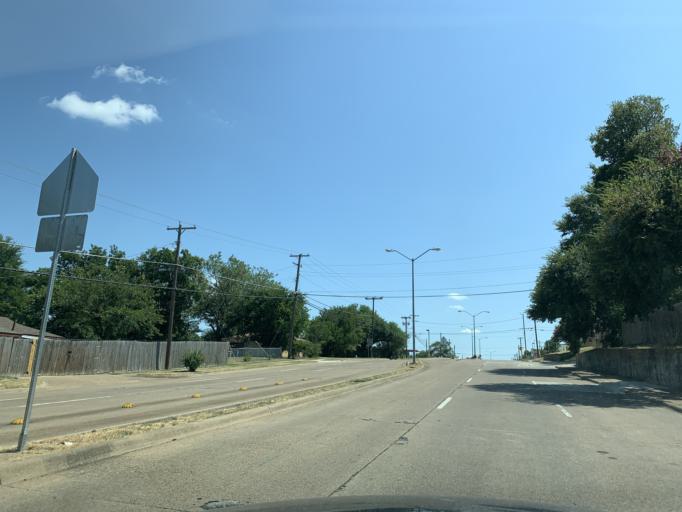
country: US
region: Texas
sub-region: Dallas County
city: Hutchins
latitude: 32.6772
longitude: -96.8059
